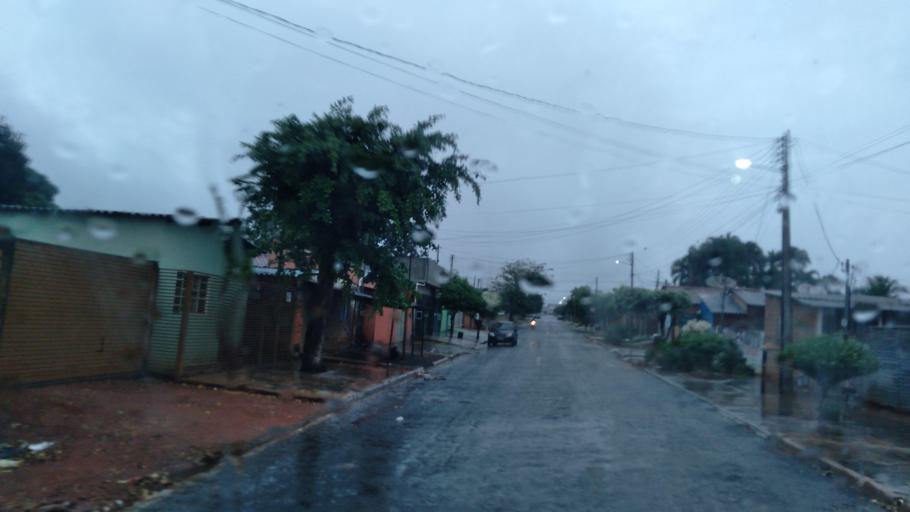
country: BR
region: Goias
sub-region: Mineiros
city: Mineiros
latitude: -17.5404
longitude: -52.5455
